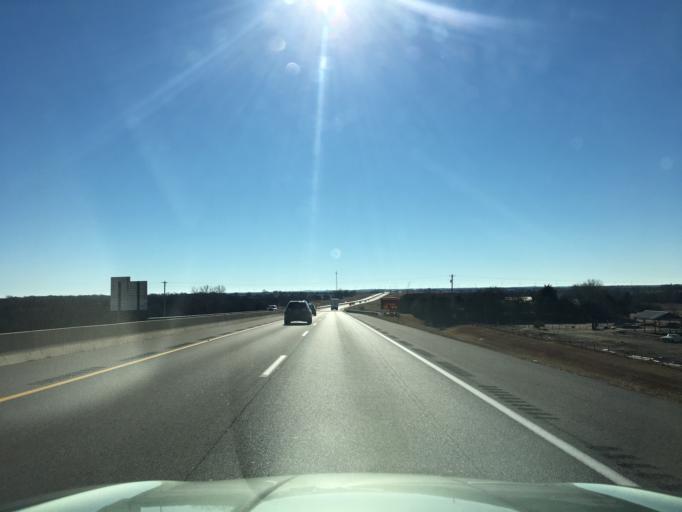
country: US
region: Kansas
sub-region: Sumner County
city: Wellington
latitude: 37.2632
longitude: -97.3397
